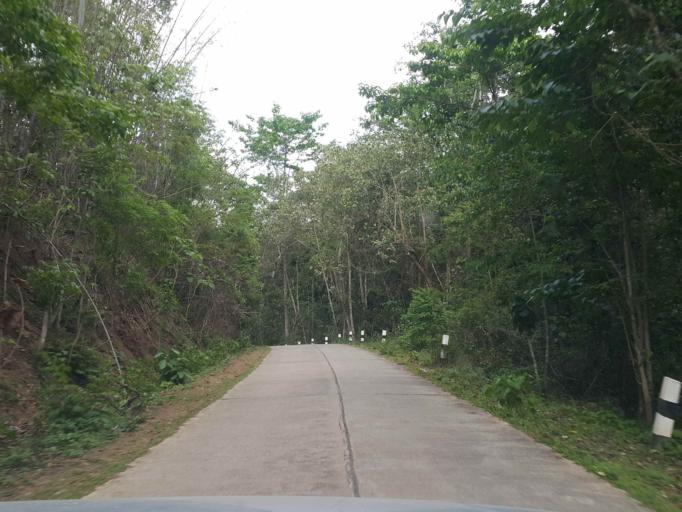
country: TH
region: Chiang Mai
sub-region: Amphoe Chiang Dao
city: Chiang Dao
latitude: 19.4110
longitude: 98.7933
